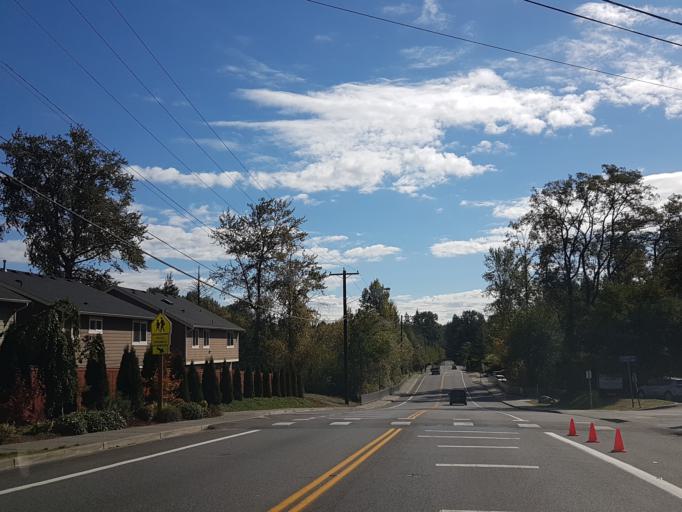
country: US
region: Washington
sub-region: Snohomish County
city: Brier
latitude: 47.7798
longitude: -122.2559
